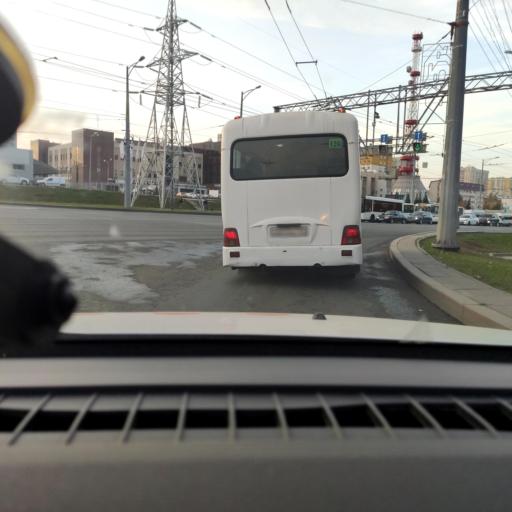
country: RU
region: Samara
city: Samara
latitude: 53.2161
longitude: 50.1855
